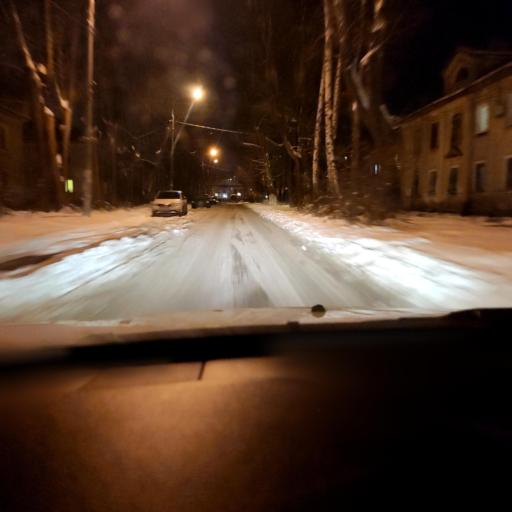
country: RU
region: Samara
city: Petra-Dubrava
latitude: 53.3024
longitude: 50.2870
